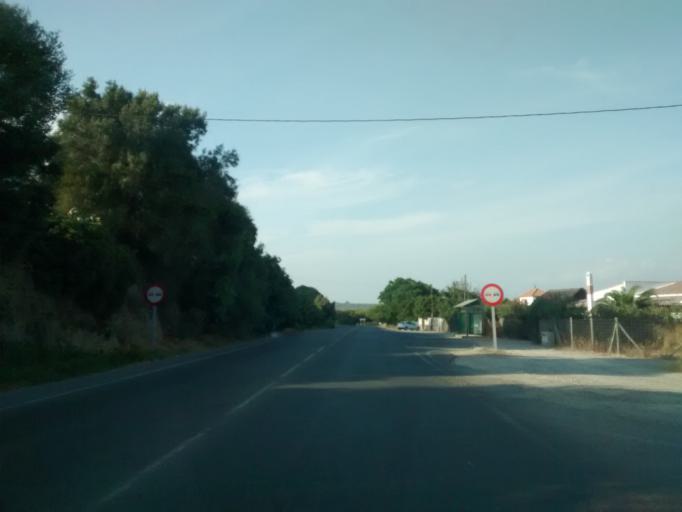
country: ES
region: Andalusia
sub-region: Provincia de Cadiz
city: Vejer de la Frontera
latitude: 36.2244
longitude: -5.9486
